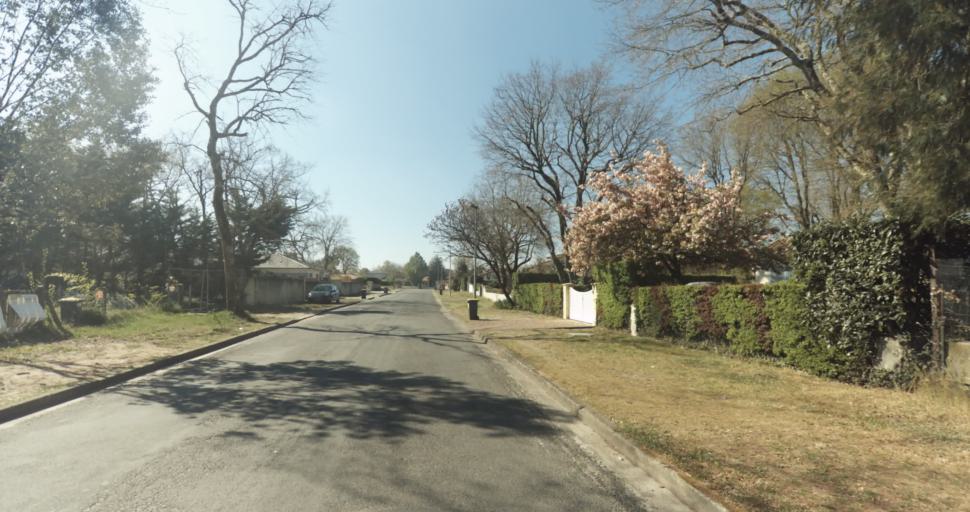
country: FR
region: Aquitaine
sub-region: Departement de la Gironde
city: Martignas-sur-Jalle
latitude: 44.8054
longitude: -0.7829
